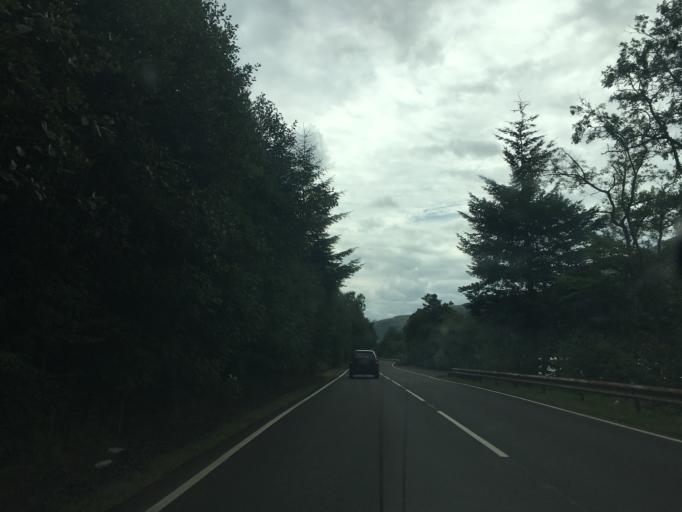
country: GB
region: Scotland
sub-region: Stirling
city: Callander
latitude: 56.2874
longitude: -4.2839
